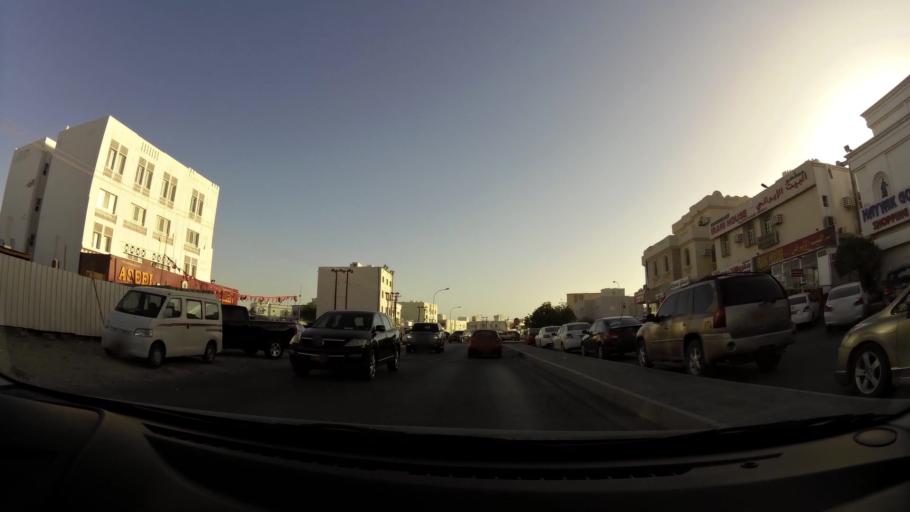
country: OM
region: Muhafazat Masqat
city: As Sib al Jadidah
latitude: 23.6051
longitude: 58.2249
